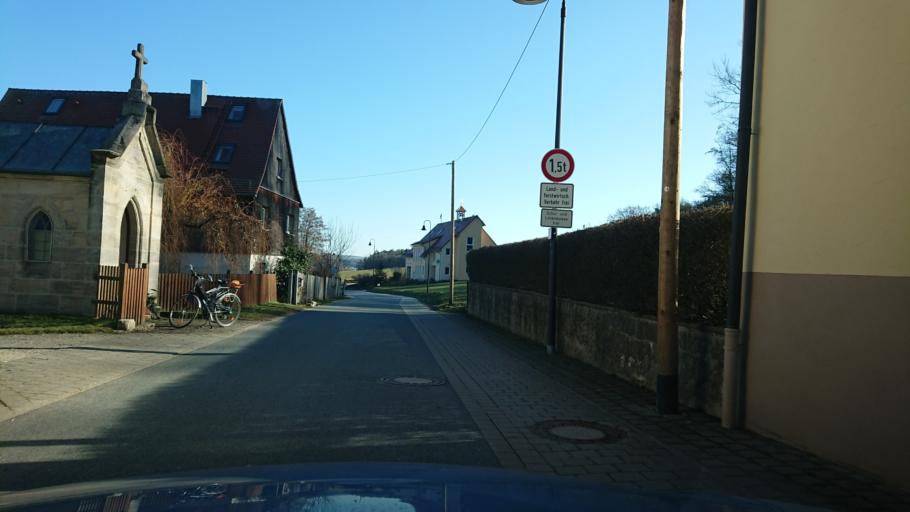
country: DE
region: Bavaria
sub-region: Upper Franconia
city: Neunkirchen am Brand
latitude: 49.6237
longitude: 11.1073
